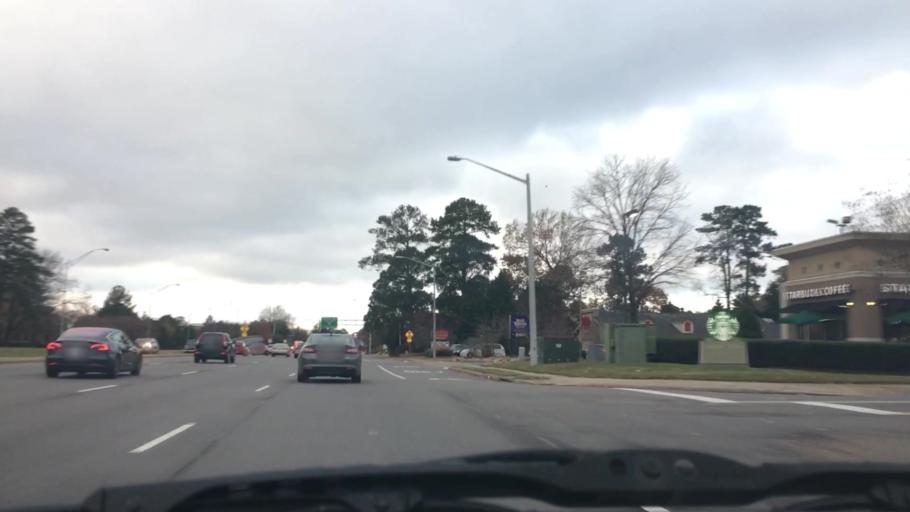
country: US
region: Virginia
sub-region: City of Chesapeake
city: Chesapeake
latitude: 36.8283
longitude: -76.1338
